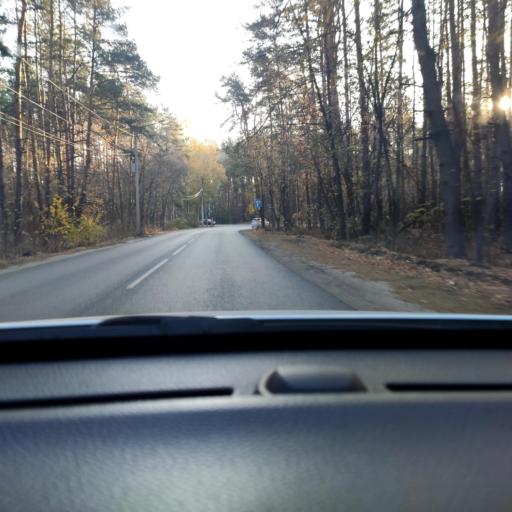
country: RU
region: Voronezj
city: Voronezh
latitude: 51.6845
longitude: 39.2815
